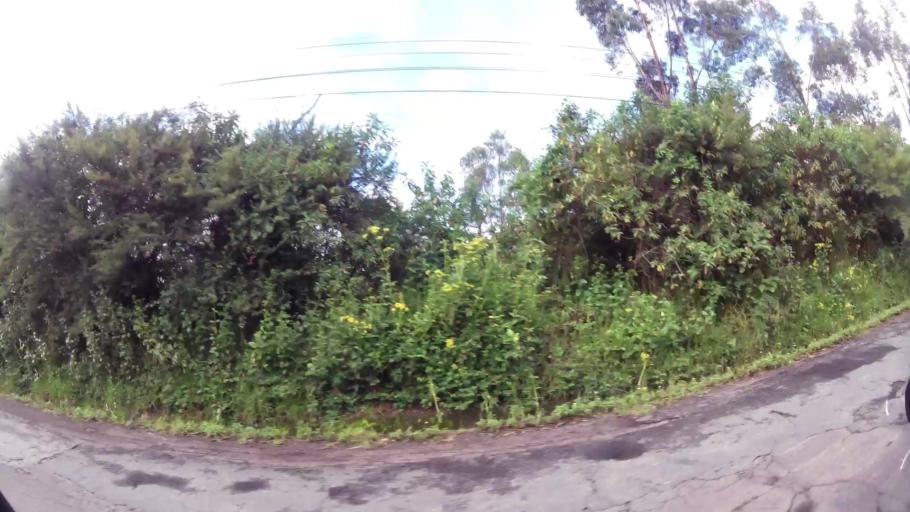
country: EC
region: Pichincha
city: Sangolqui
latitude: -0.3150
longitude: -78.4062
